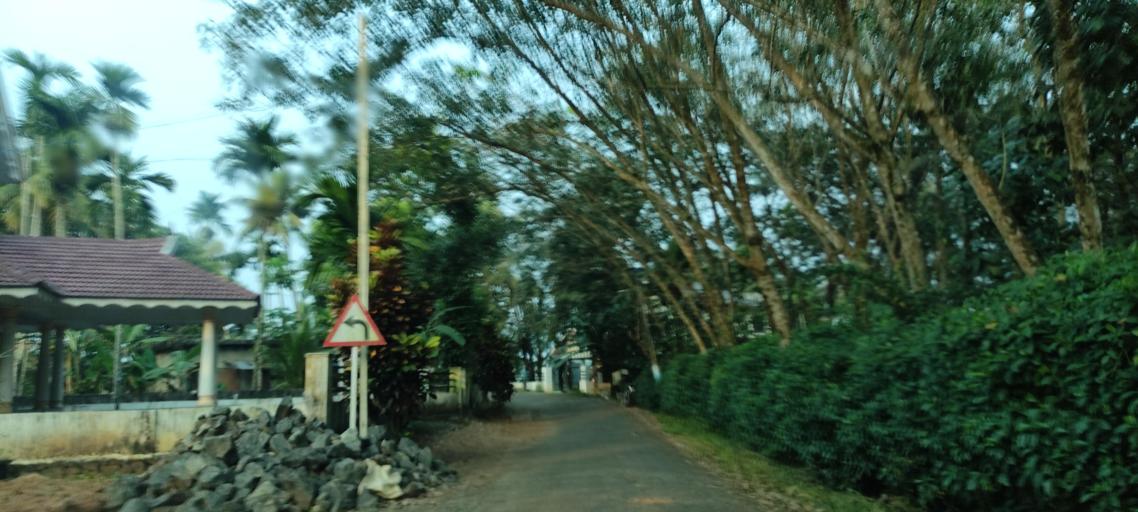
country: IN
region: Kerala
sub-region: Kottayam
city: Vaikam
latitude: 9.6834
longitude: 76.4656
